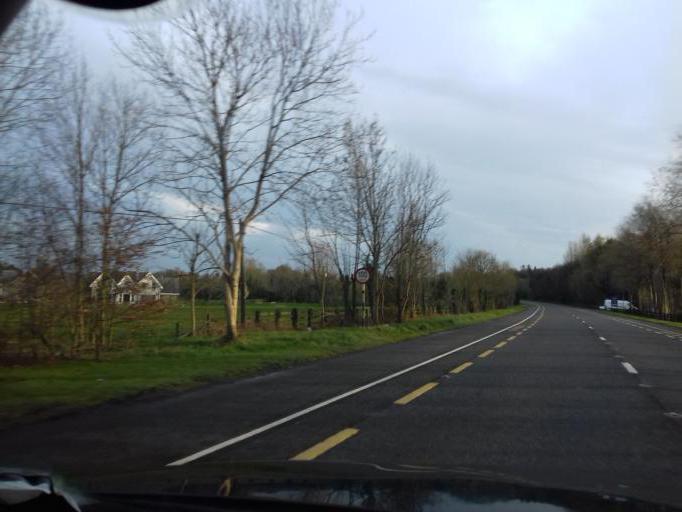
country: IE
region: Leinster
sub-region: Laois
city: Abbeyleix
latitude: 52.8782
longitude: -7.3628
